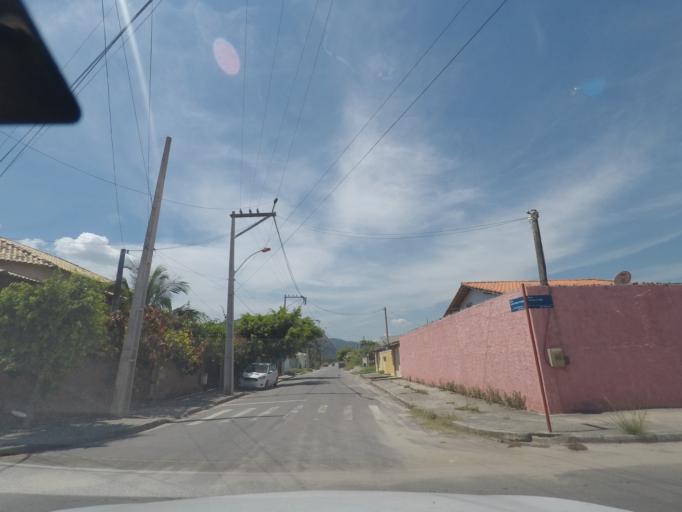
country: BR
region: Rio de Janeiro
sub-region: Marica
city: Marica
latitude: -22.9621
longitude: -42.9576
